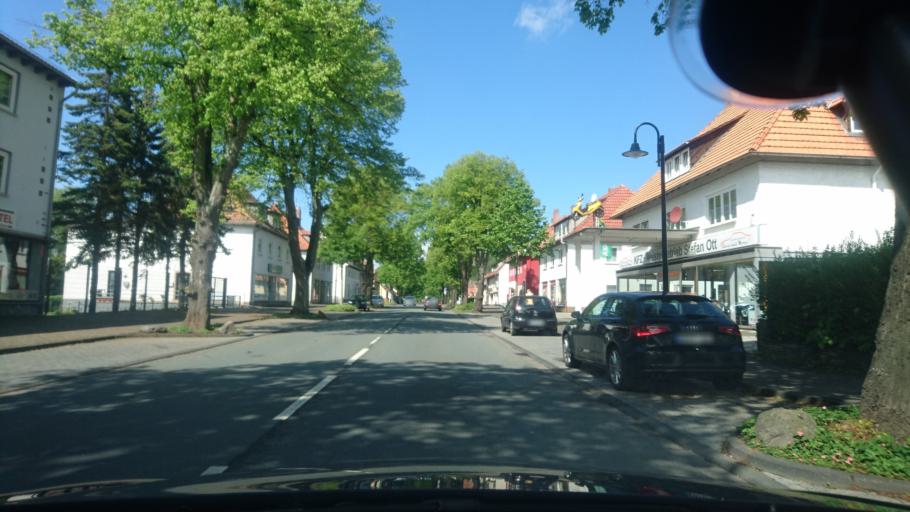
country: DE
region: Hesse
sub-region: Regierungsbezirk Kassel
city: Bad Arolsen
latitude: 51.3814
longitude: 9.0043
